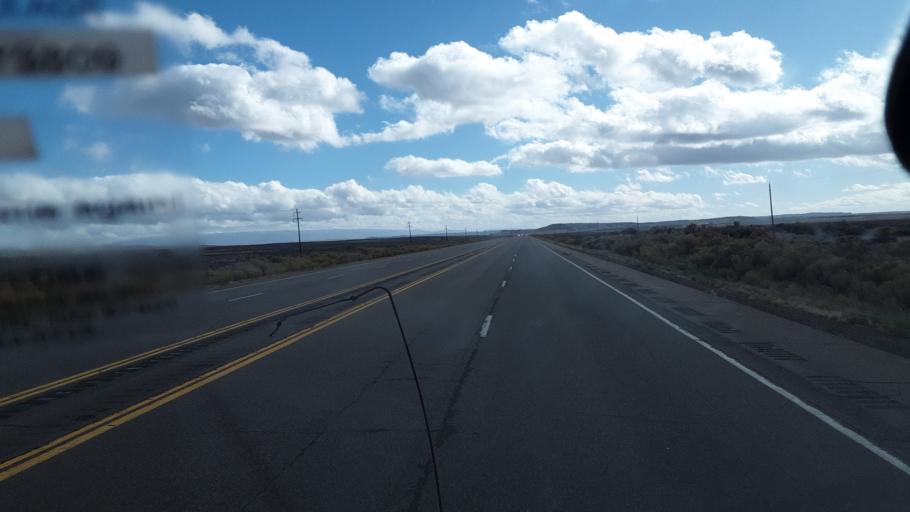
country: US
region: New Mexico
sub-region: Rio Arriba County
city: Santa Teresa
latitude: 36.1653
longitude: -107.3094
